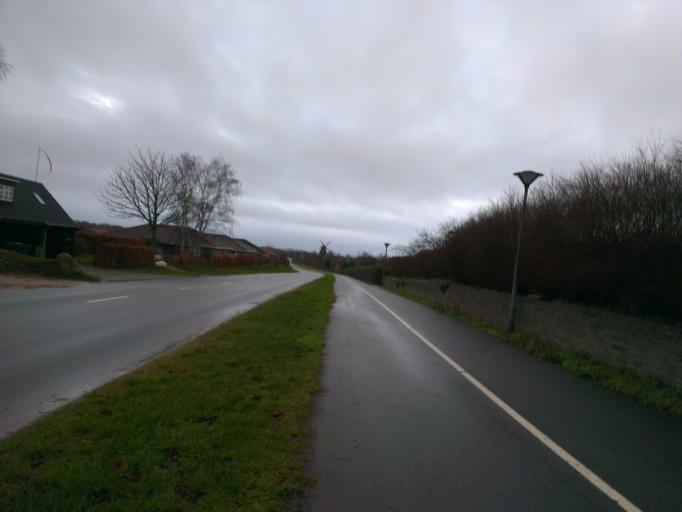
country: DK
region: Capital Region
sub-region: Frederikssund Kommune
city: Jaegerspris
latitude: 55.8484
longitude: 11.9973
